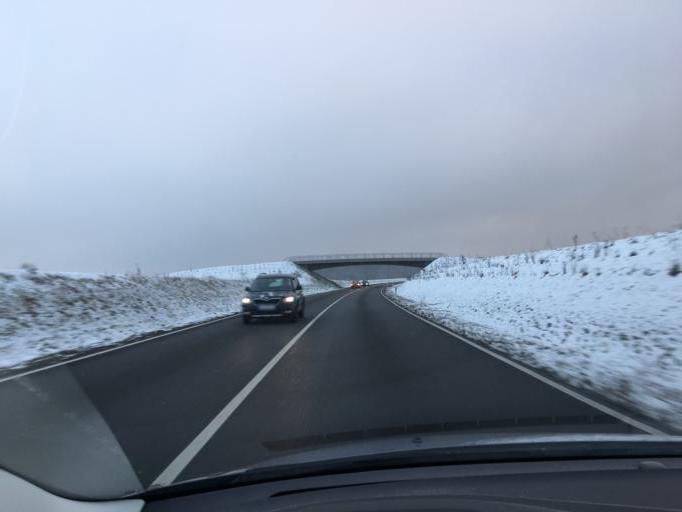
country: DE
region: Saxony
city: Grossposna
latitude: 51.2493
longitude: 12.4813
